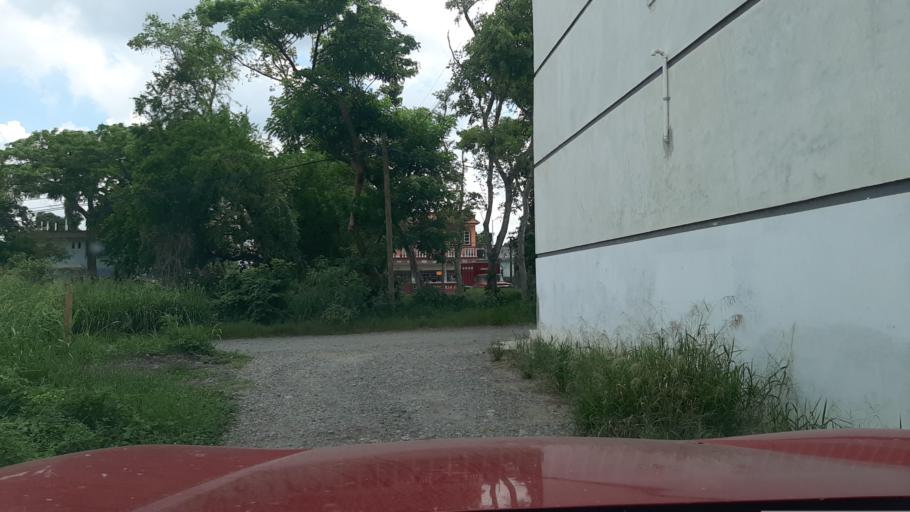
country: MX
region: Veracruz
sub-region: Poza Rica de Hidalgo
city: Villa de las Flores
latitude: 20.5737
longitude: -97.4323
